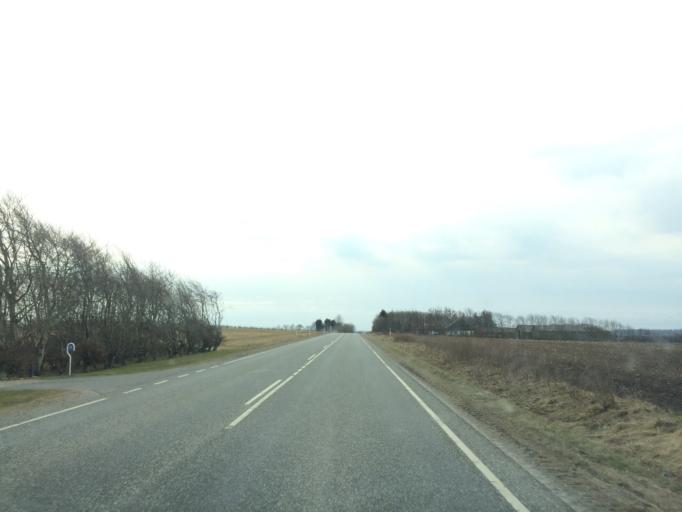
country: DK
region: Central Jutland
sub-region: Ringkobing-Skjern Kommune
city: Videbaek
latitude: 56.0825
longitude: 8.5070
